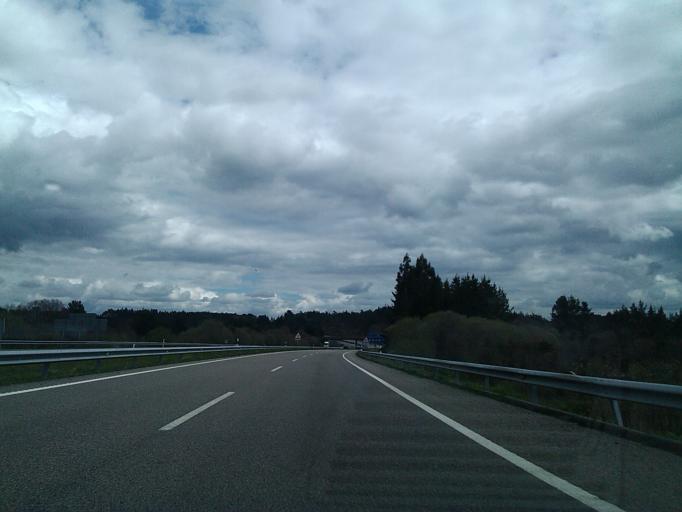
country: ES
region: Galicia
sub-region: Provincia de Lugo
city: Guitiriz
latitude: 43.1882
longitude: -7.9188
